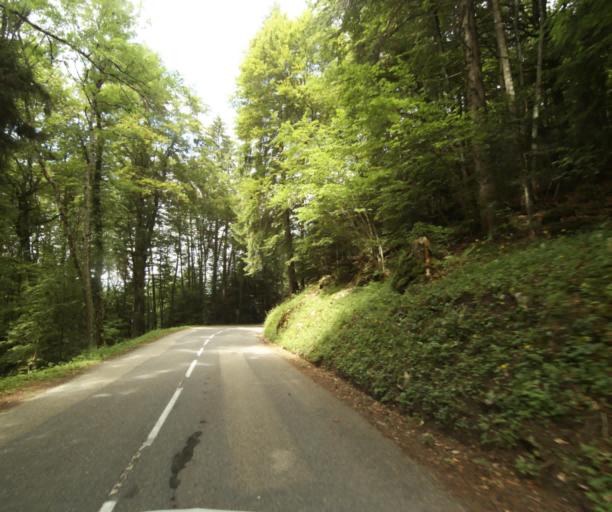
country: FR
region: Rhone-Alpes
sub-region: Departement de la Haute-Savoie
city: Perrignier
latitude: 46.2823
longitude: 6.4574
